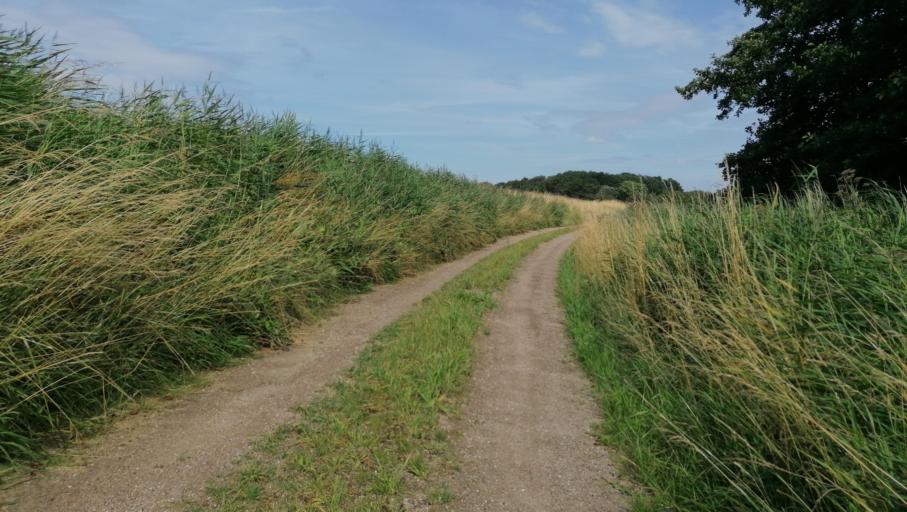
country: DK
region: Zealand
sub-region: Odsherred Kommune
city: Horve
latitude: 55.7887
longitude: 11.4231
